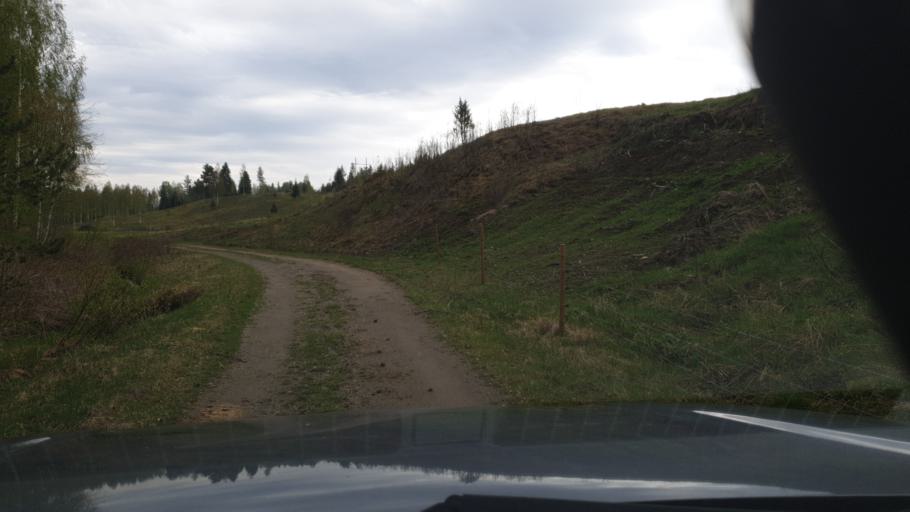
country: SE
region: Gaevleborg
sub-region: Ljusdals Kommun
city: Jaervsoe
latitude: 61.7368
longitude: 16.2809
